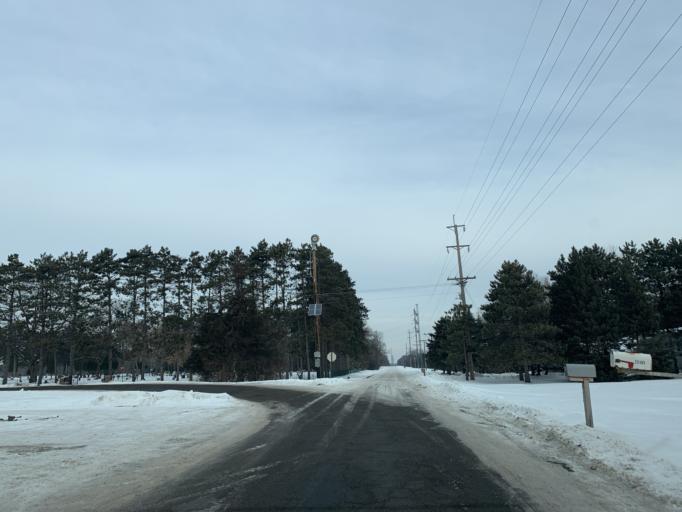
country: US
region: Minnesota
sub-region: Washington County
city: Forest Lake
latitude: 45.2858
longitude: -93.0090
